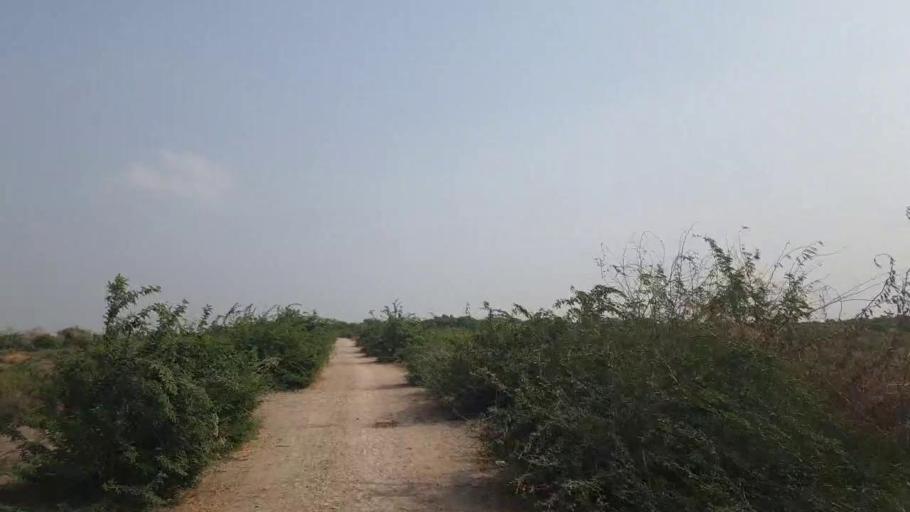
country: PK
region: Sindh
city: Badin
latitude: 24.5475
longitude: 68.6958
